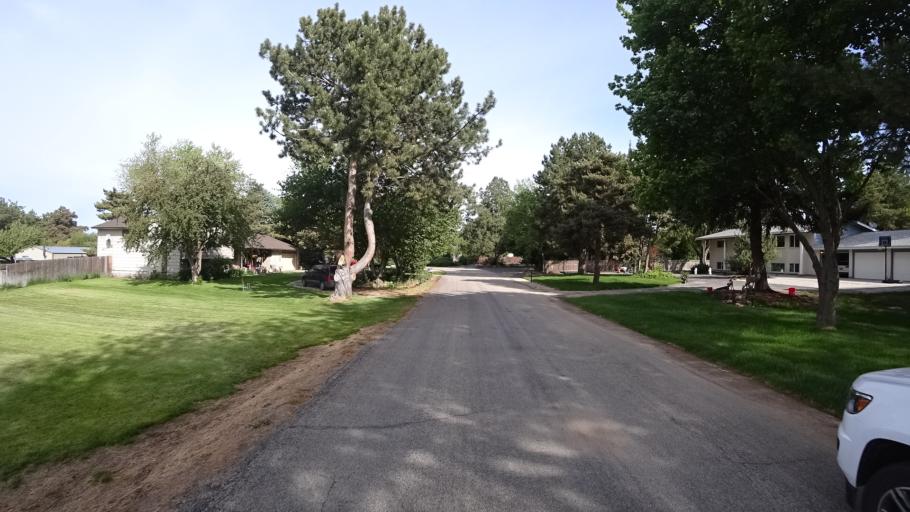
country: US
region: Idaho
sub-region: Ada County
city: Garden City
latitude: 43.5662
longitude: -116.2988
